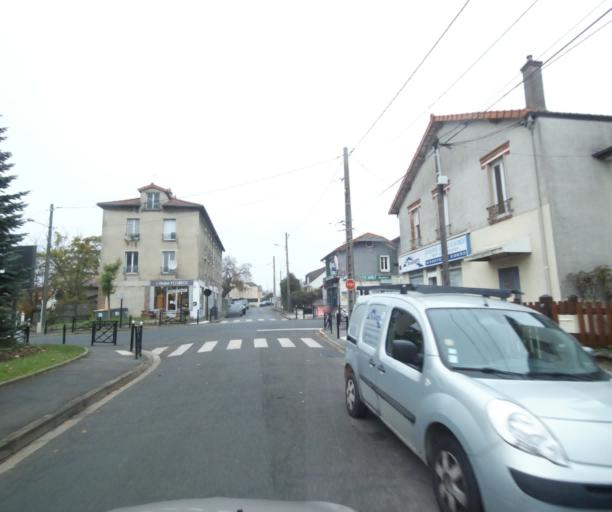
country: FR
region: Ile-de-France
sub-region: Departement de Seine-Saint-Denis
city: Gagny
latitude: 48.8753
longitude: 2.5453
